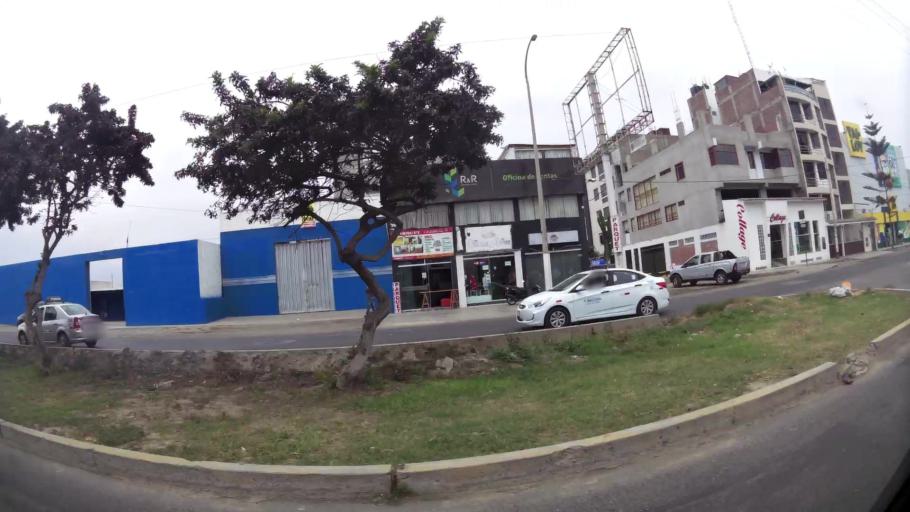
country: PE
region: La Libertad
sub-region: Provincia de Trujillo
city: Buenos Aires
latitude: -8.1332
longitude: -79.0351
